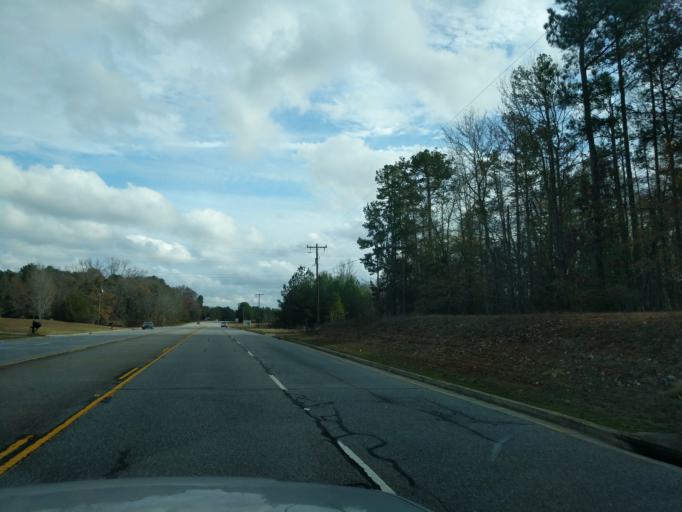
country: US
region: South Carolina
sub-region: Greenwood County
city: Ware Shoals
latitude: 34.4361
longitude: -82.2458
